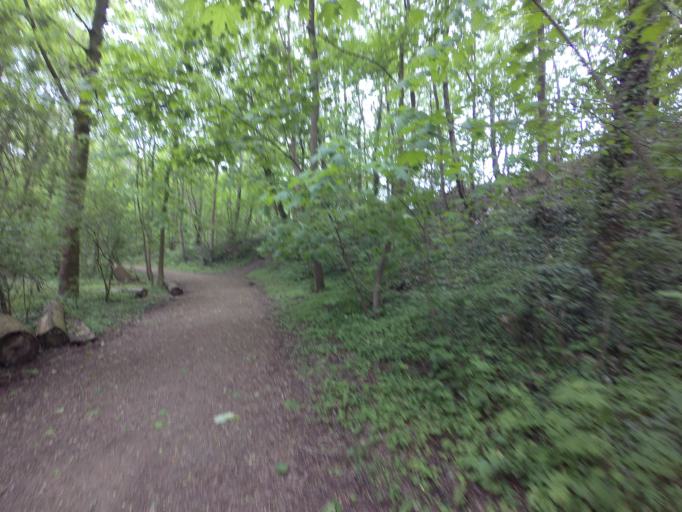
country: DE
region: North Rhine-Westphalia
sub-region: Regierungsbezirk Koln
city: Herzogenrath
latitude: 50.8949
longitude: 6.1193
